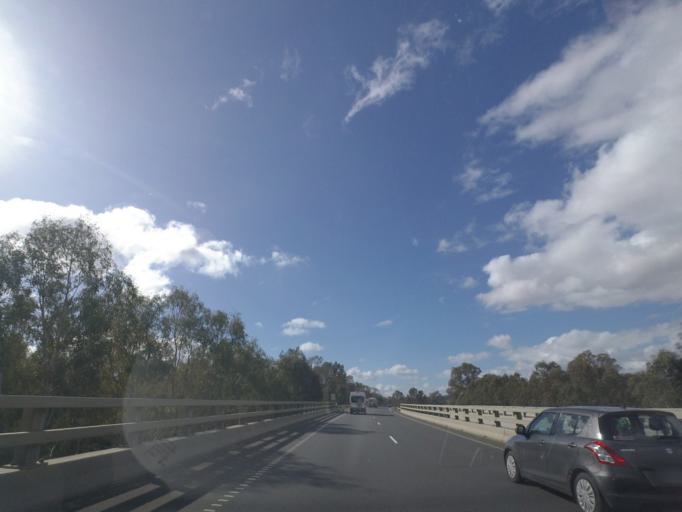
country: AU
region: New South Wales
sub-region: Albury Municipality
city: South Albury
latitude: -36.1024
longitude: 146.9069
